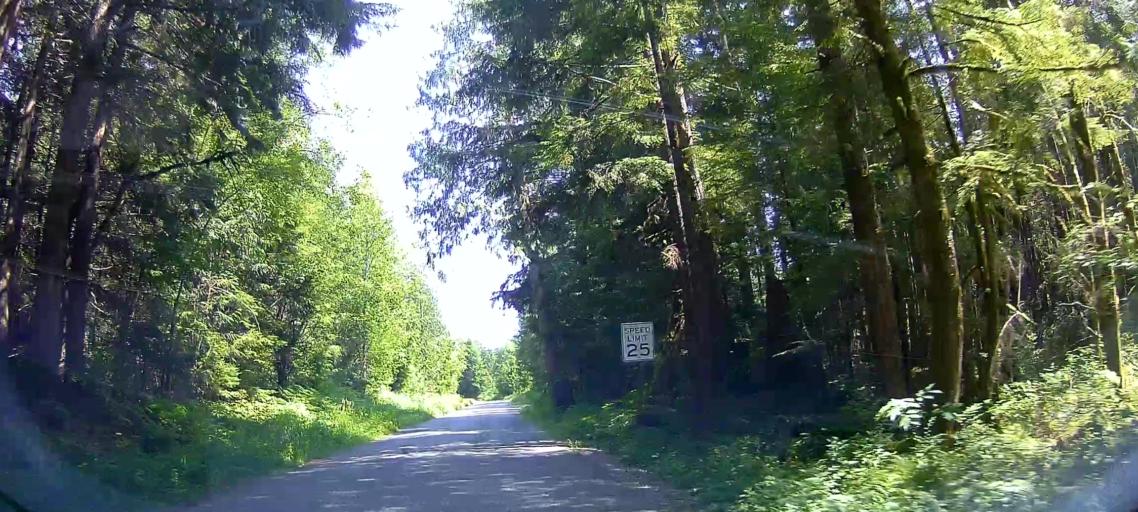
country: US
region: Washington
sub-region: Snohomish County
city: Arlington Heights
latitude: 48.3354
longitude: -122.0212
